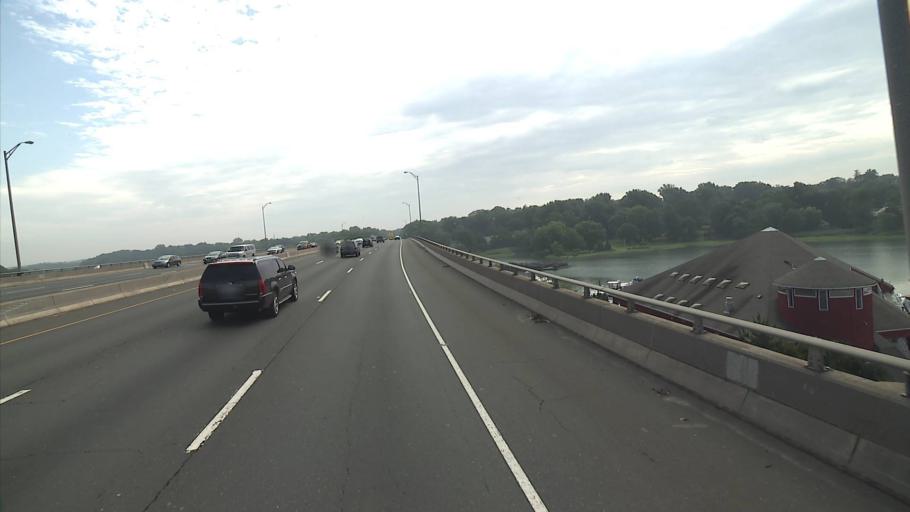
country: US
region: Connecticut
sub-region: Fairfield County
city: Cos Cob
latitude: 41.0355
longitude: -73.5945
